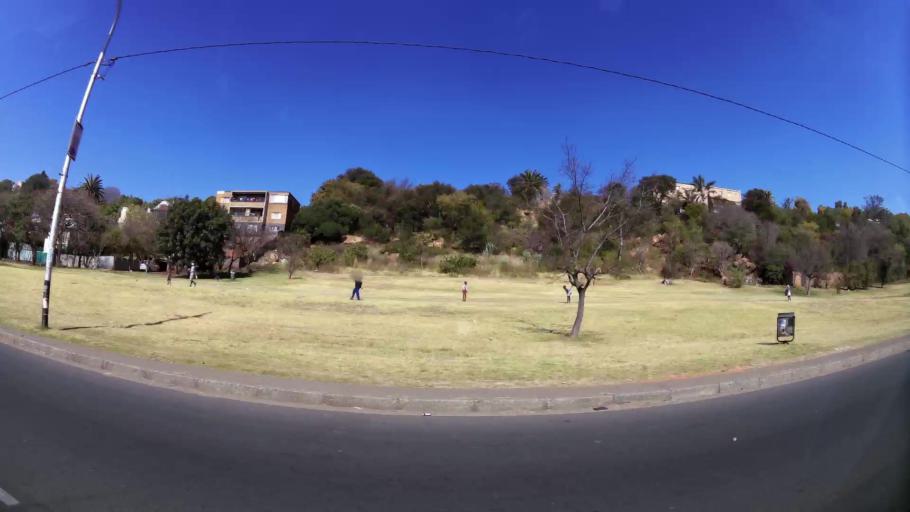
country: ZA
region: Gauteng
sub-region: City of Johannesburg Metropolitan Municipality
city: Johannesburg
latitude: -26.1963
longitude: 28.0712
